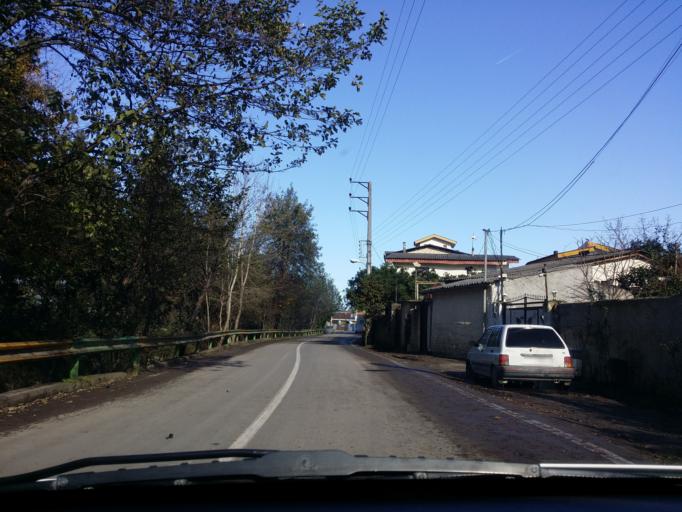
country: IR
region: Mazandaran
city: Chalus
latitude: 36.6847
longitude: 51.3134
